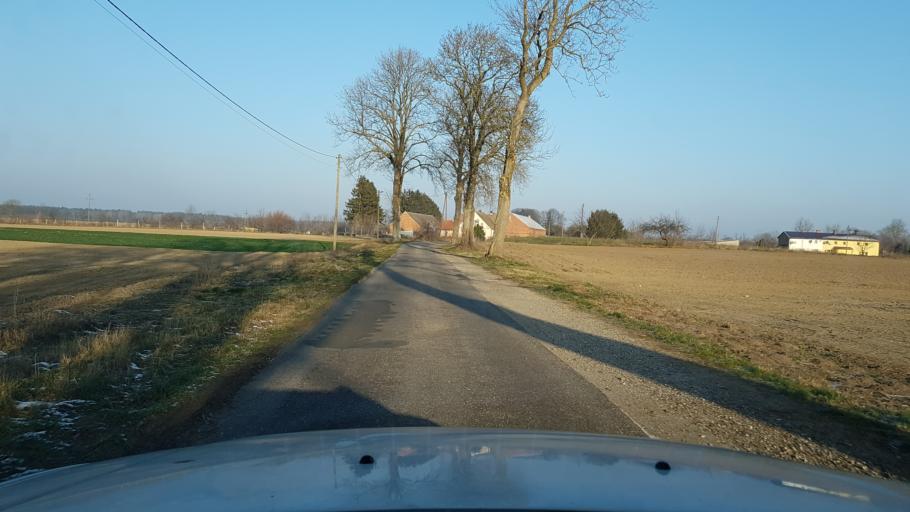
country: PL
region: West Pomeranian Voivodeship
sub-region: Powiat bialogardzki
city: Bialogard
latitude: 54.0704
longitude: 16.0869
